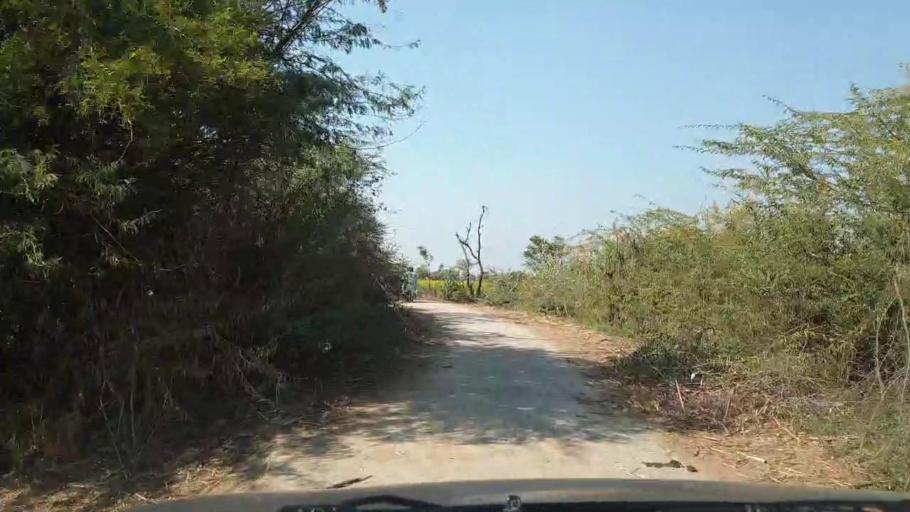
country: PK
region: Sindh
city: Jhol
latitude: 25.9113
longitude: 68.8235
